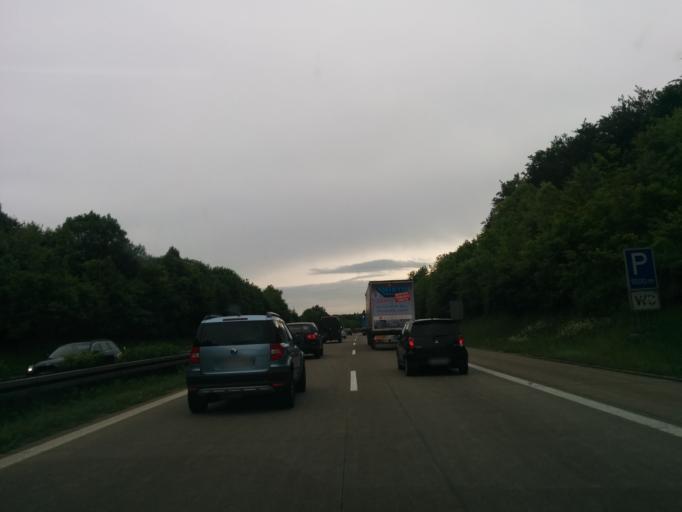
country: DE
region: Baden-Wuerttemberg
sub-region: Regierungsbezirk Stuttgart
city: Nattheim
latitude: 48.7292
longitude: 10.2003
